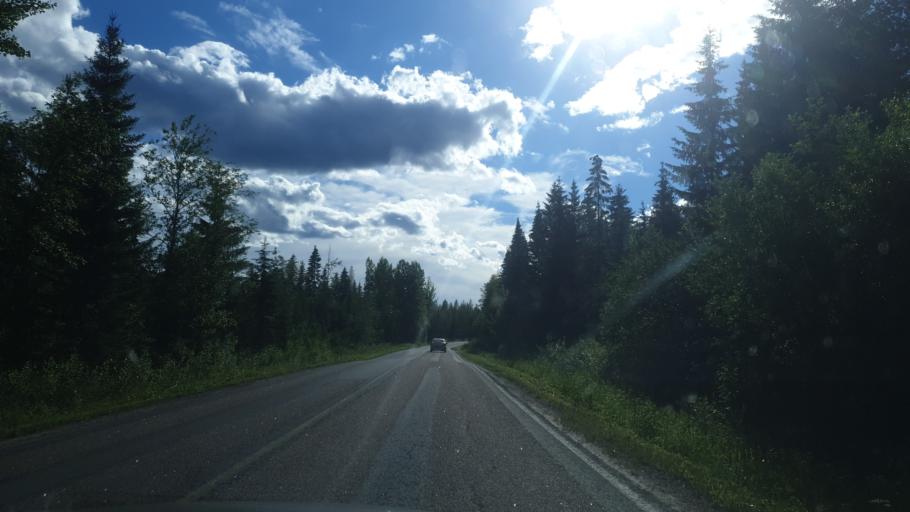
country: FI
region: Southern Savonia
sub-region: Mikkeli
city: Pertunmaa
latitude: 61.5228
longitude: 26.5800
